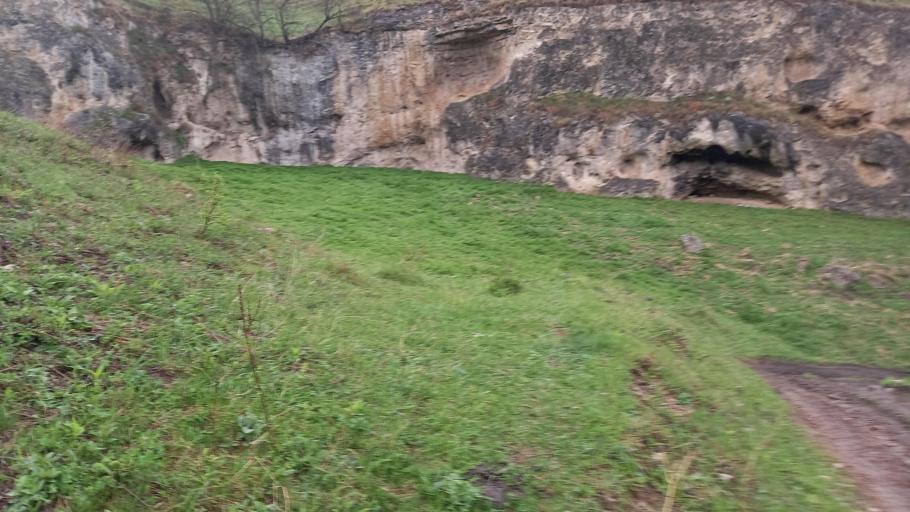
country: RU
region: Kabardino-Balkariya
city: Bylym
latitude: 43.5917
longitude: 43.0252
